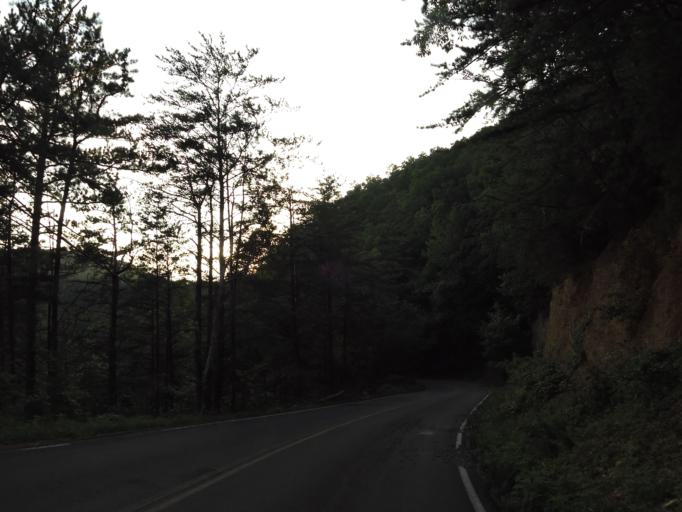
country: US
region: Tennessee
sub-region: Blount County
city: Maryville
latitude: 35.6291
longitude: -83.9414
